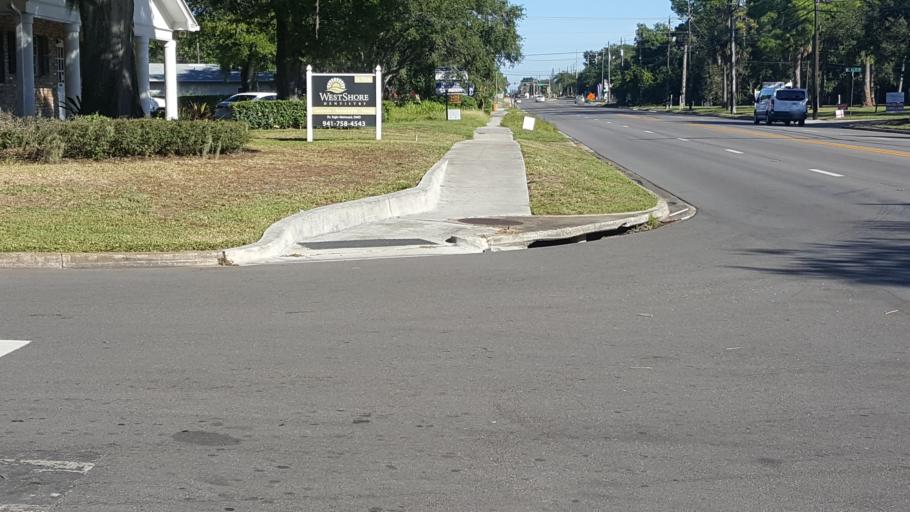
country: US
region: Florida
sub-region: Manatee County
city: South Bradenton
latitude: 27.4562
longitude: -82.5877
